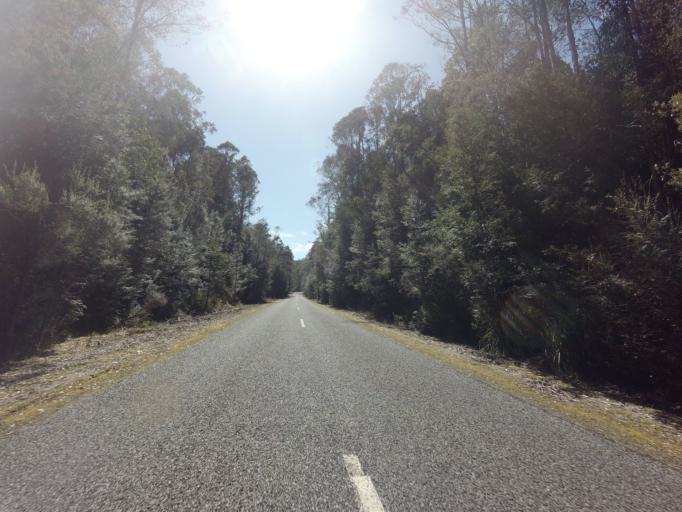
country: AU
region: Tasmania
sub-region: Derwent Valley
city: New Norfolk
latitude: -42.7390
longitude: 146.4210
